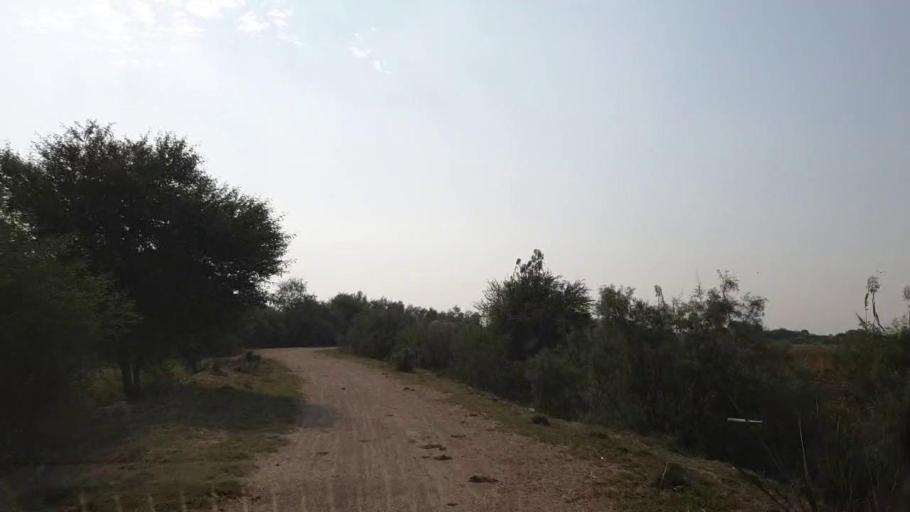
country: PK
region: Sindh
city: Tando Muhammad Khan
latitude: 25.0711
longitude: 68.4319
